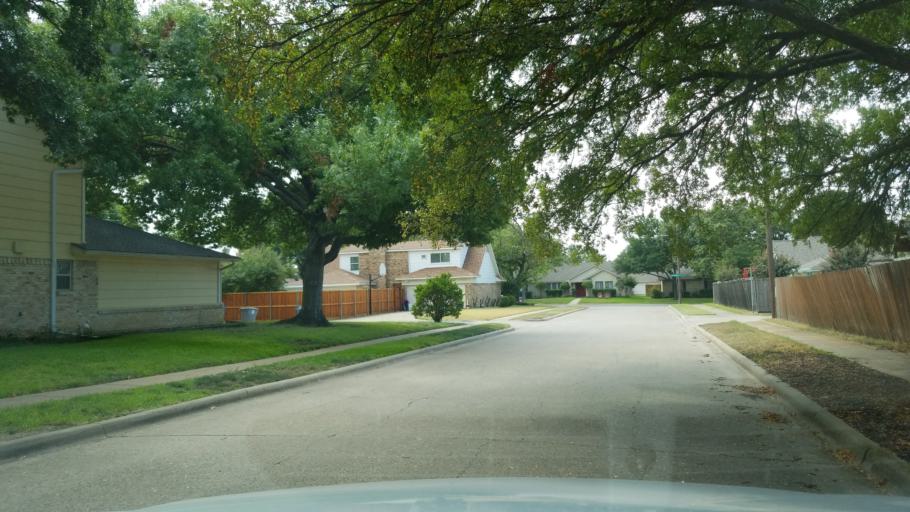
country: US
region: Texas
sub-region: Dallas County
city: Richardson
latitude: 32.9678
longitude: -96.7760
